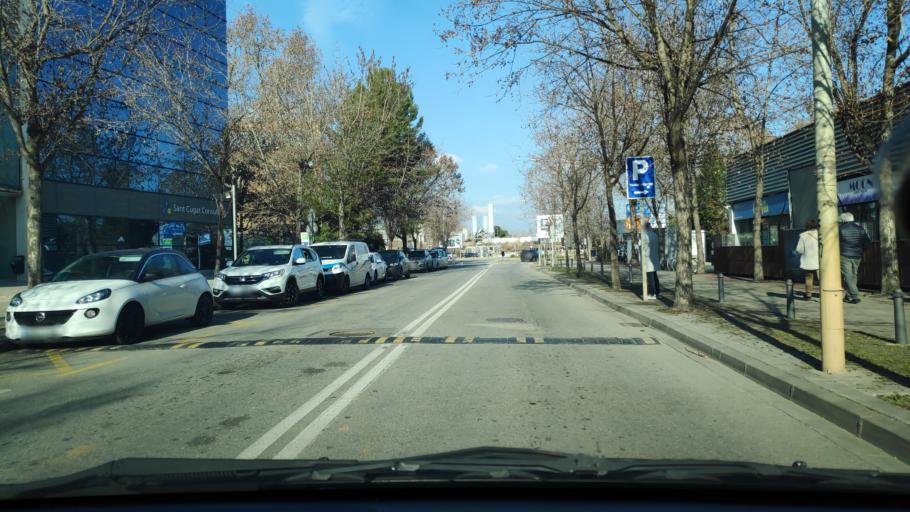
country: ES
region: Catalonia
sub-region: Provincia de Barcelona
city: Sant Cugat del Valles
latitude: 41.4748
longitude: 2.0976
